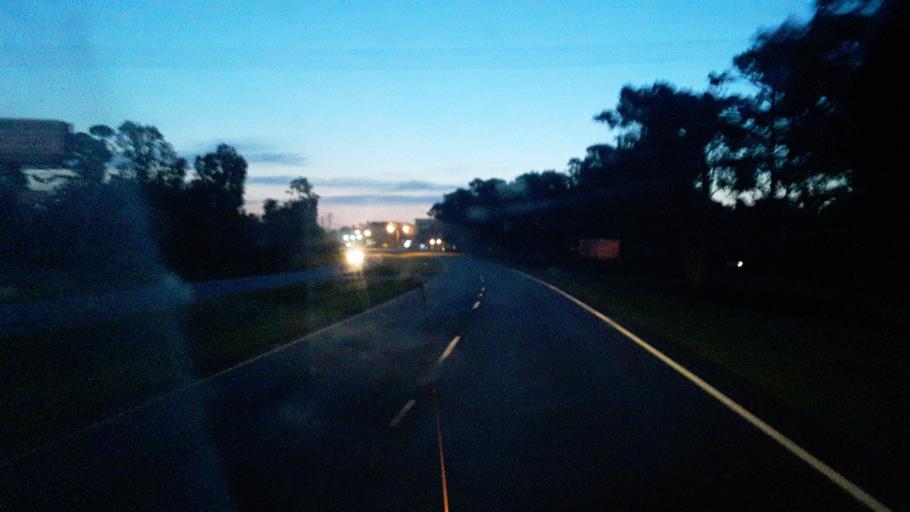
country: US
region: South Carolina
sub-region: Horry County
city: Little River
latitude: 33.8684
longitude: -78.6308
